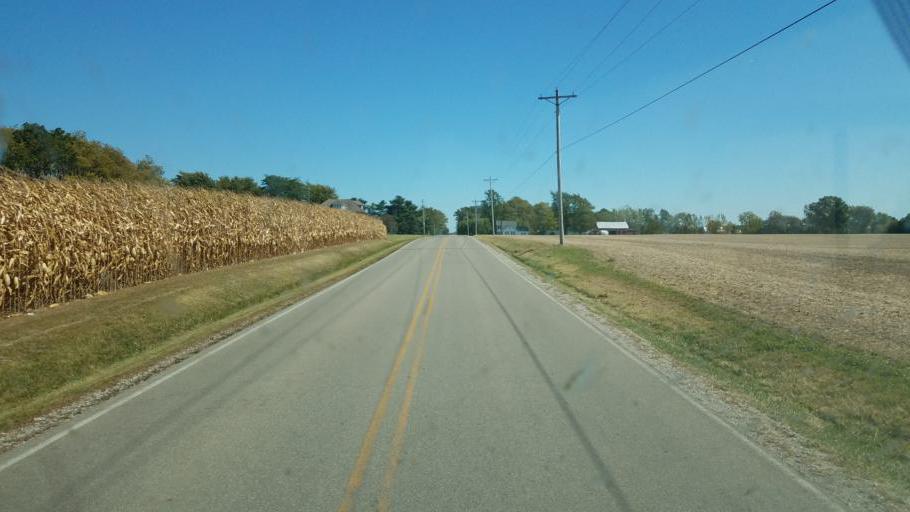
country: US
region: Ohio
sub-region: Huron County
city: Willard
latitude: 40.9819
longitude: -82.7905
